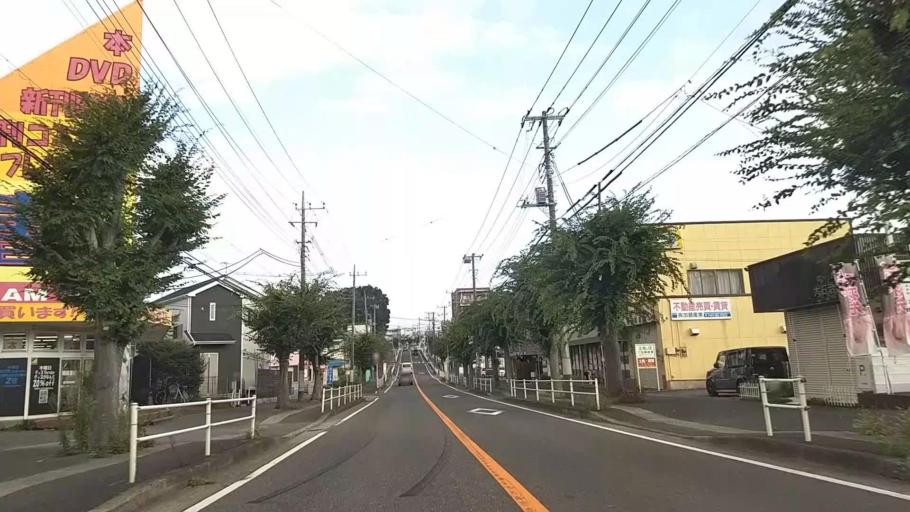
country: JP
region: Kanagawa
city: Isehara
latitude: 35.3956
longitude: 139.3012
